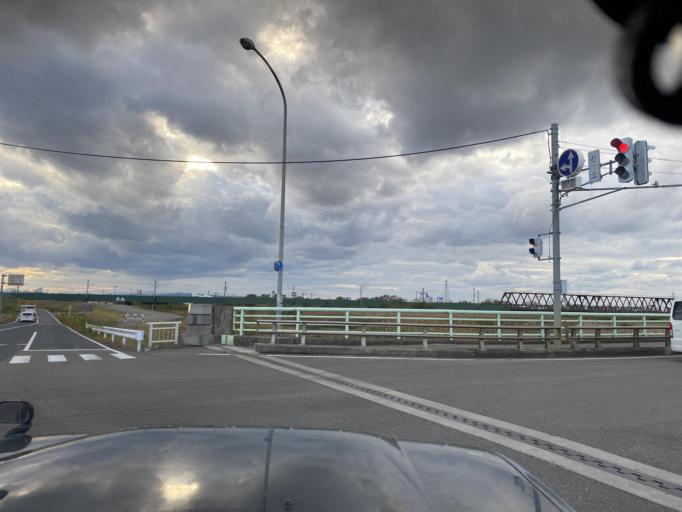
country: JP
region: Niigata
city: Sanjo
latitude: 37.6438
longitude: 138.9500
